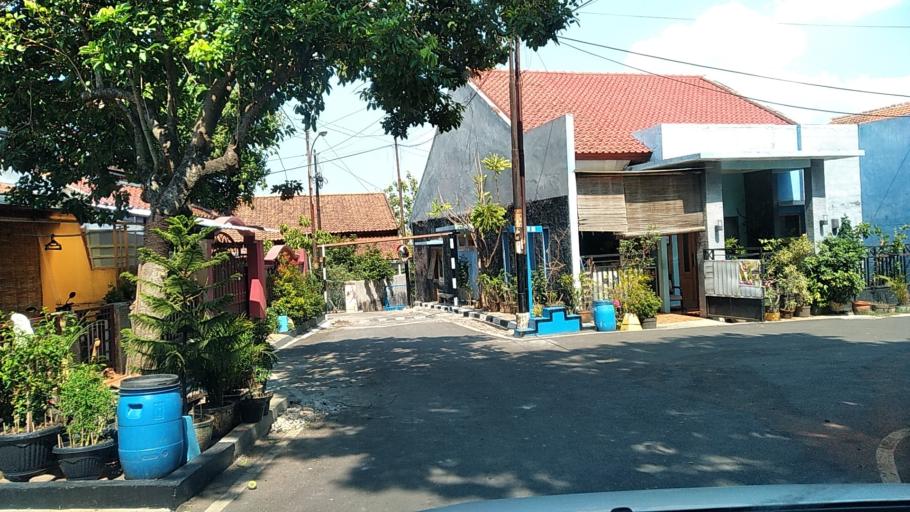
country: ID
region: Central Java
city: Ungaran
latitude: -7.0745
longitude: 110.4329
